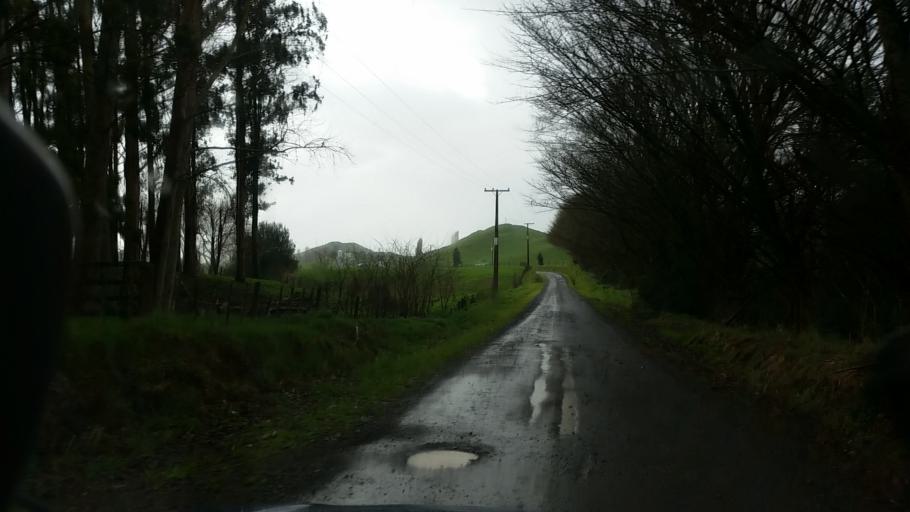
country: NZ
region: Taranaki
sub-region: South Taranaki District
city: Eltham
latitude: -39.3558
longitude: 174.4343
